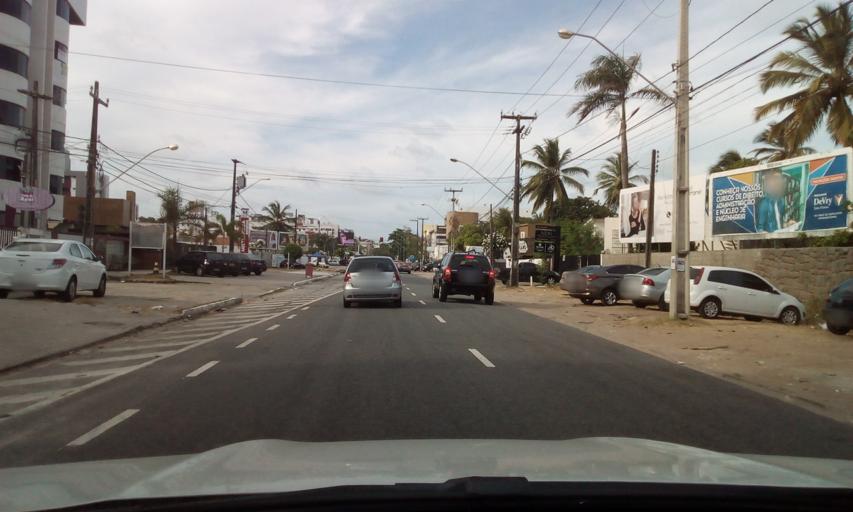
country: BR
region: Paraiba
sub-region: Joao Pessoa
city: Joao Pessoa
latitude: -7.0957
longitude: -34.8346
